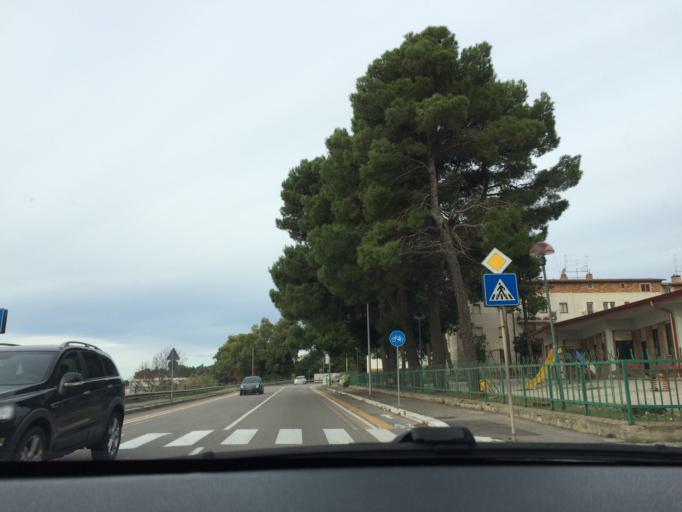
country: IT
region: Basilicate
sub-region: Provincia di Matera
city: Matera
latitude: 40.6582
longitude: 16.6044
